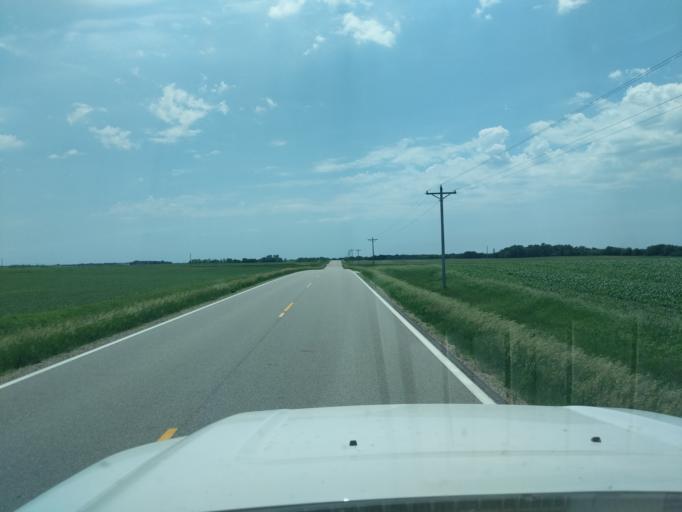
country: US
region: Minnesota
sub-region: Yellow Medicine County
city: Granite Falls
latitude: 44.7629
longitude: -95.4020
